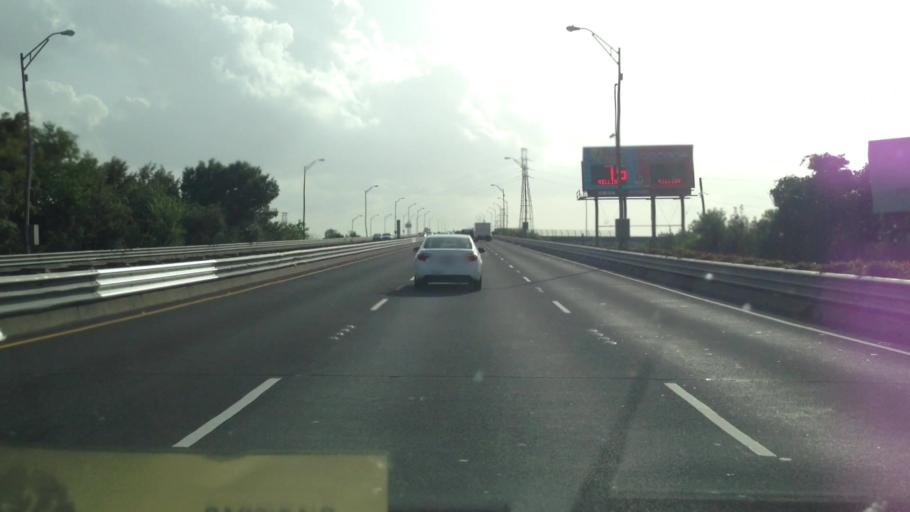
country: US
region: Louisiana
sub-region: Saint Bernard Parish
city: Arabi
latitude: 30.0070
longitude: -90.0172
